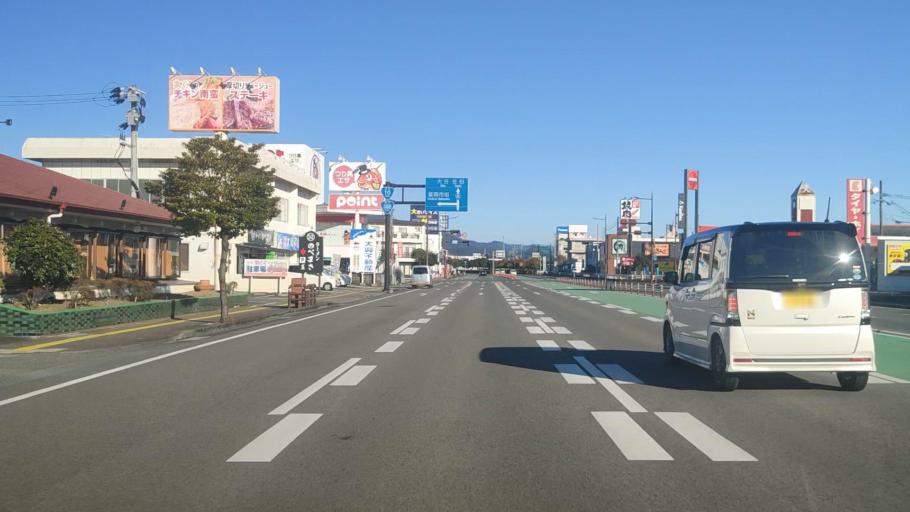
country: JP
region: Miyazaki
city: Nobeoka
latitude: 32.5748
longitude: 131.6835
